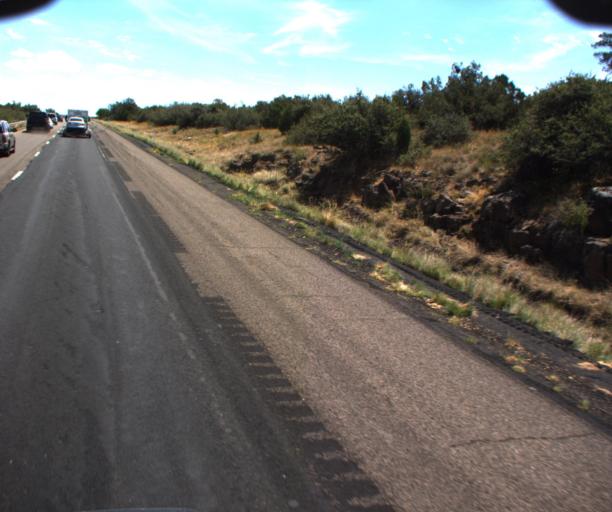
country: US
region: Arizona
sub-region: Yavapai County
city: Village of Oak Creek (Big Park)
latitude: 34.7744
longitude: -111.6330
